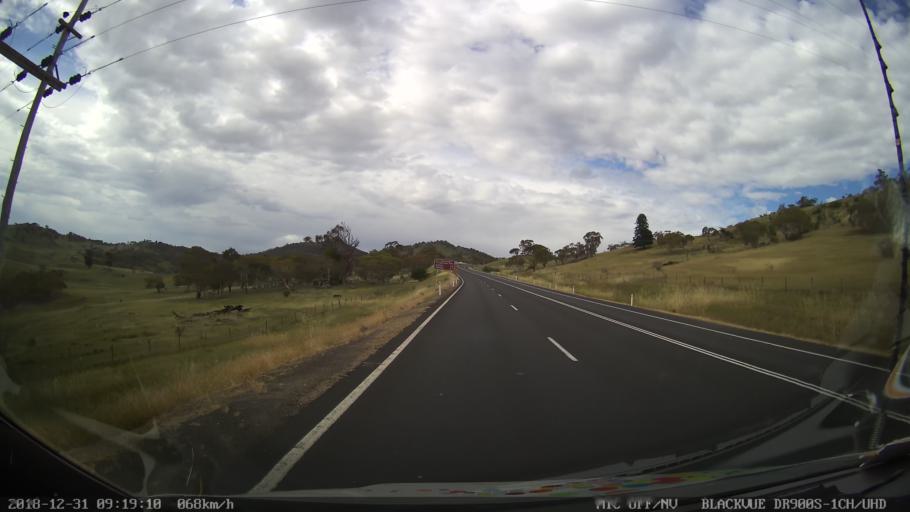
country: AU
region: New South Wales
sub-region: Snowy River
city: Jindabyne
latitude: -36.4131
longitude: 148.5875
